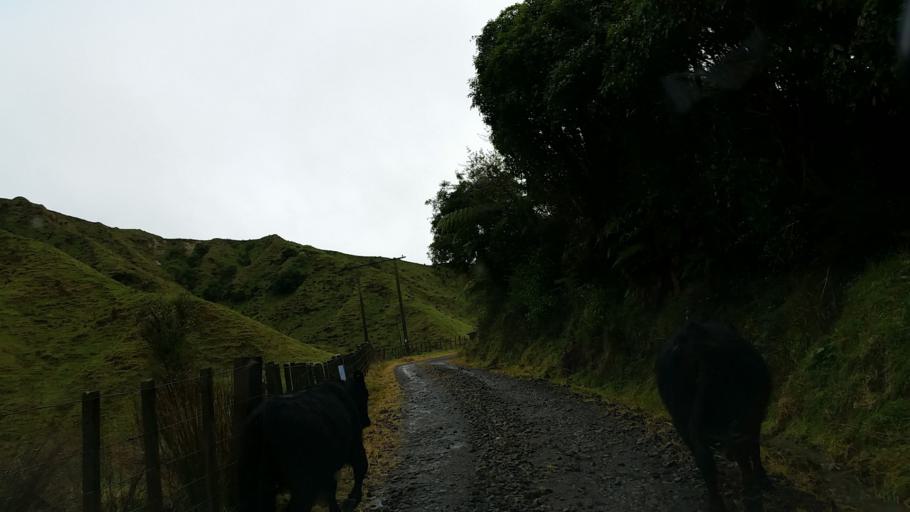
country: NZ
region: Taranaki
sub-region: South Taranaki District
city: Eltham
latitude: -39.4882
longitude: 174.4347
